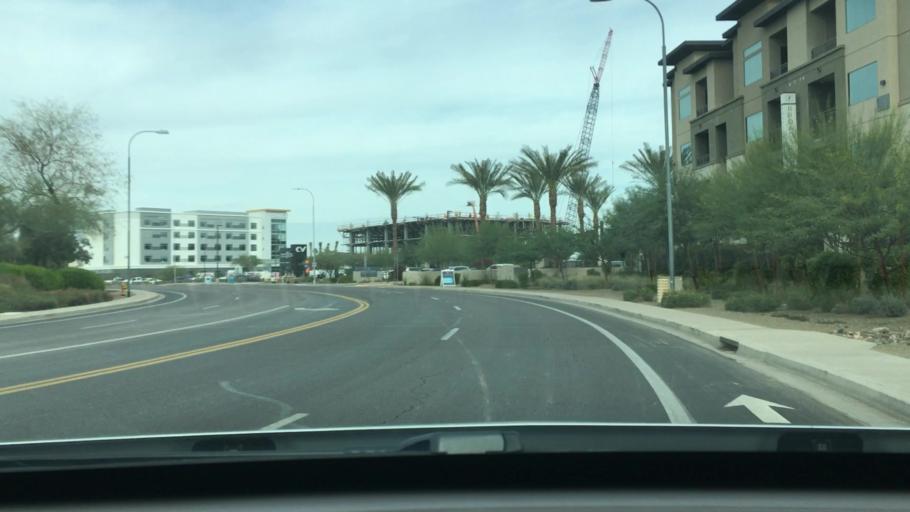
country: US
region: Arizona
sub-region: Maricopa County
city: Chandler
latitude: 33.2950
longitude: -111.8982
